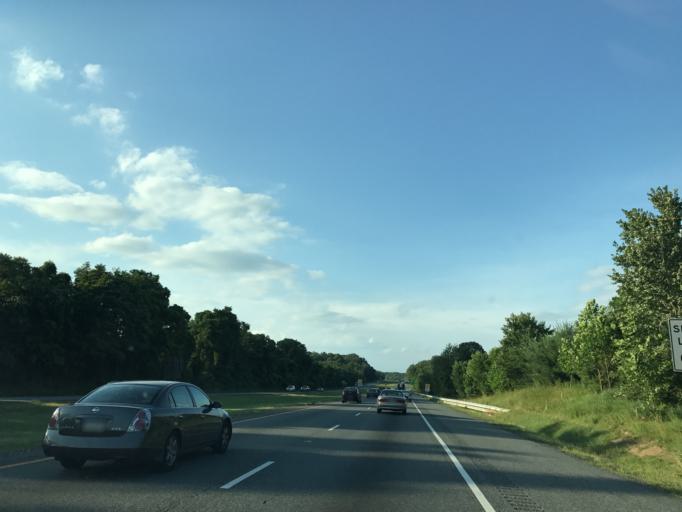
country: US
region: Pennsylvania
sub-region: York County
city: New Freedom
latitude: 39.6622
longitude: -76.6499
